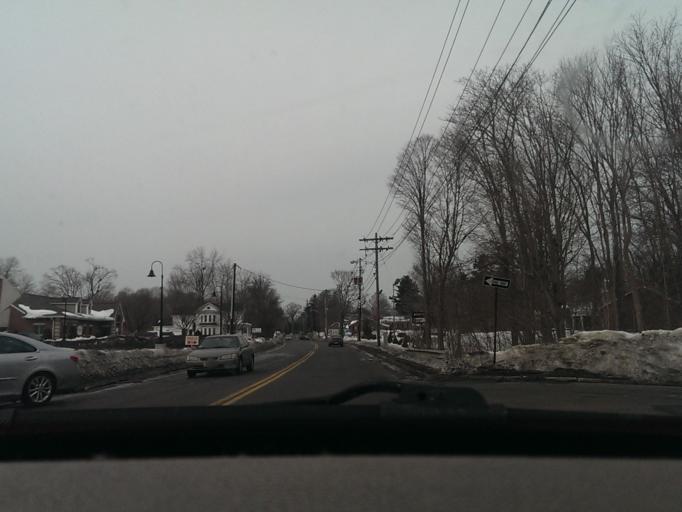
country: US
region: Massachusetts
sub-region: Hampden County
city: East Longmeadow
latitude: 42.0661
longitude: -72.5135
